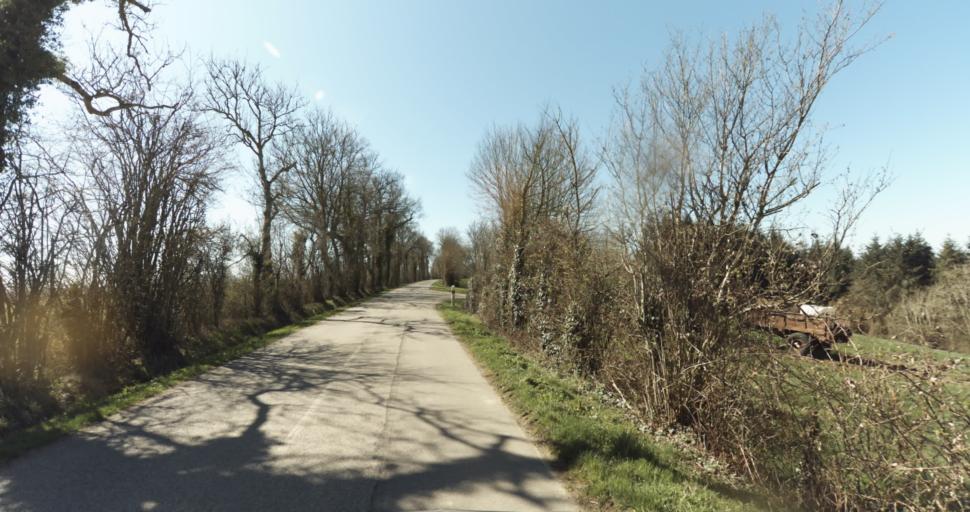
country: FR
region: Lower Normandy
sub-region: Departement de l'Orne
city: Trun
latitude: 48.9146
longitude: 0.0624
